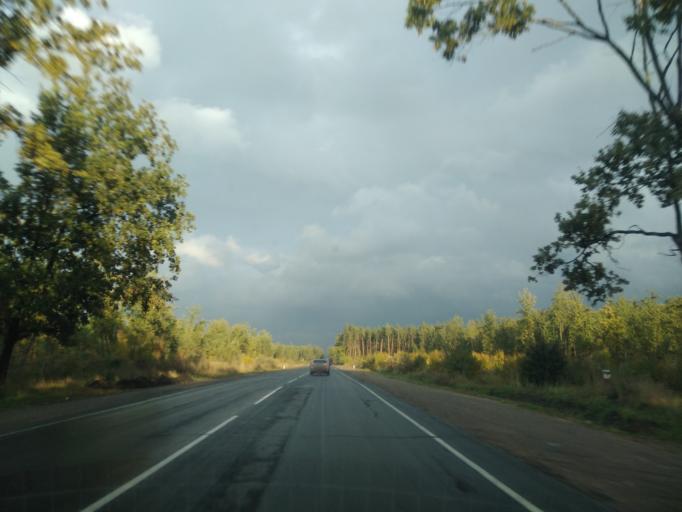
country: RU
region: Lipetsk
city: Donskoye
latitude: 52.5804
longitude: 38.9599
